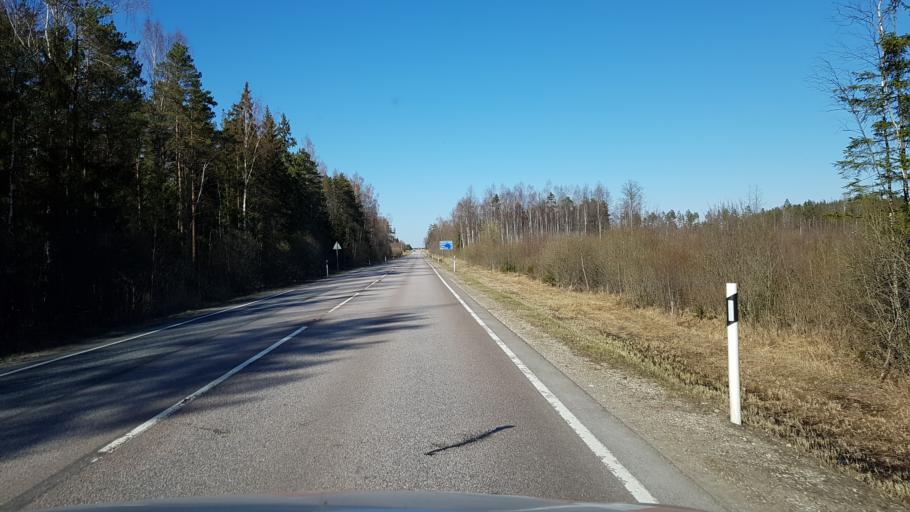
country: EE
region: Jogevamaa
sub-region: Mustvee linn
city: Mustvee
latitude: 58.7330
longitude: 26.8432
